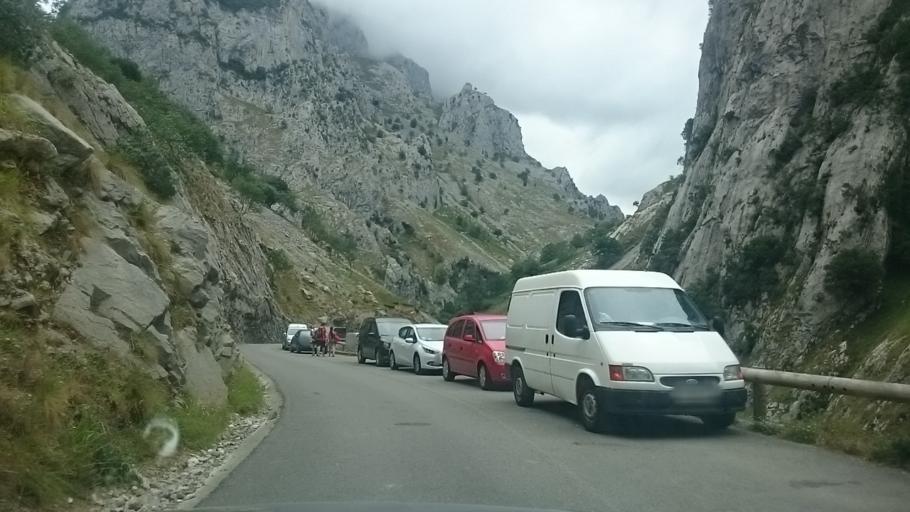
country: ES
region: Asturias
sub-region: Province of Asturias
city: Carrena
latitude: 43.2562
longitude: -4.8350
